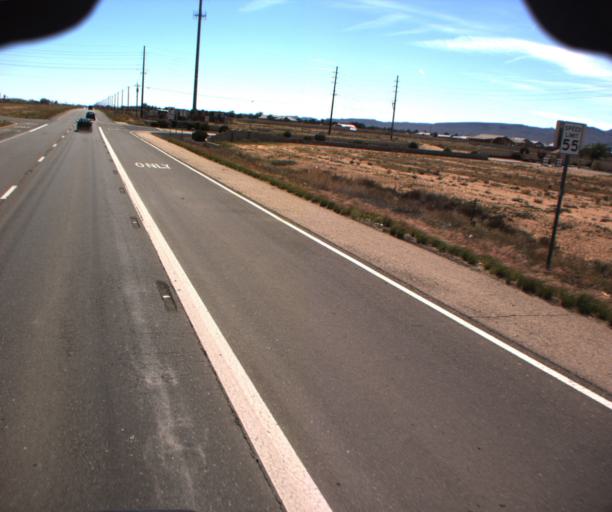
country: US
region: Arizona
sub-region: Mohave County
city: New Kingman-Butler
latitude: 35.2653
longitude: -113.9649
